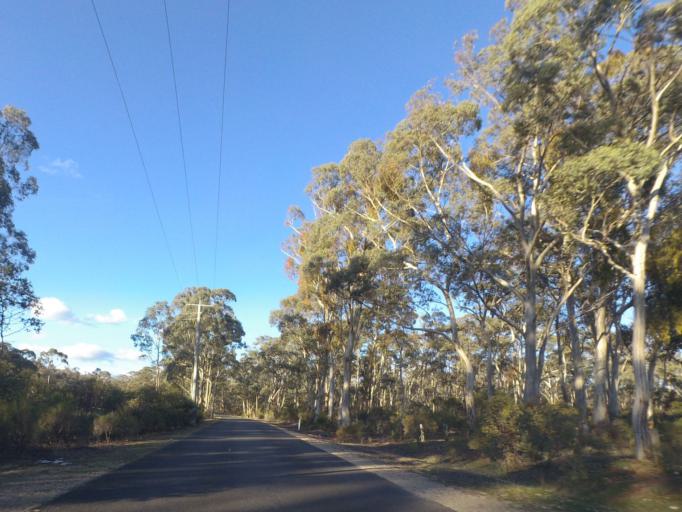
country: AU
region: Victoria
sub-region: Mount Alexander
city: Castlemaine
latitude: -37.1425
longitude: 144.1960
